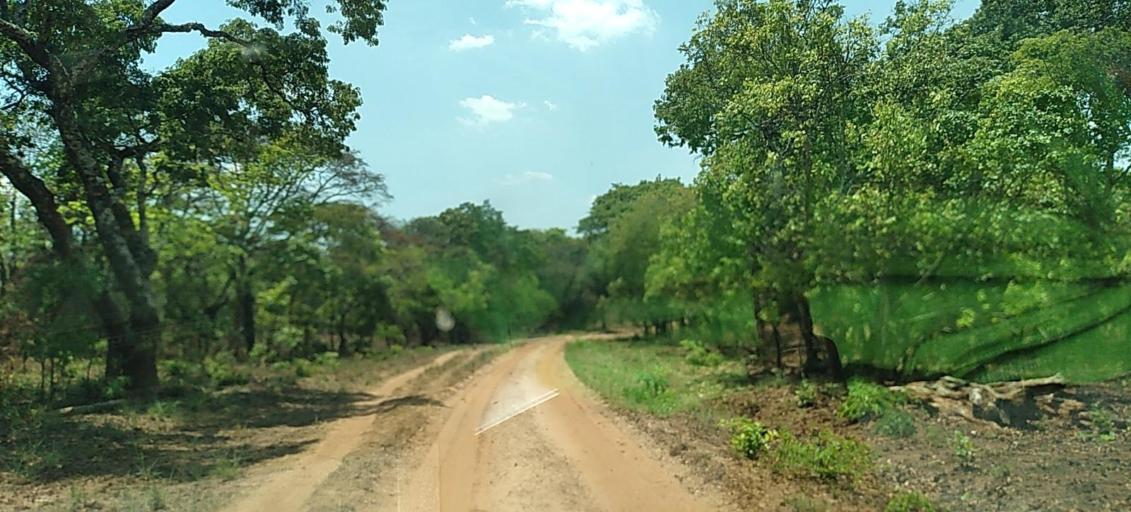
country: CD
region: Katanga
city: Kolwezi
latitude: -11.3619
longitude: 25.2062
